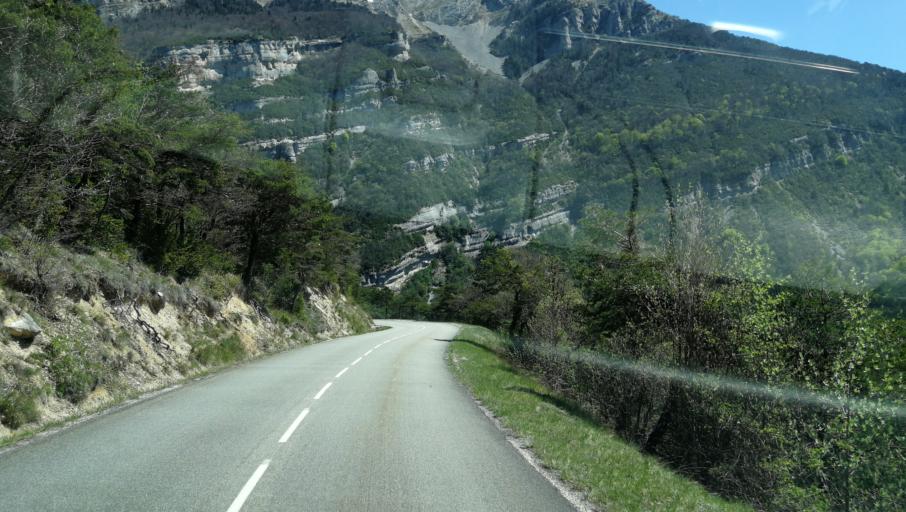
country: FR
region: Rhone-Alpes
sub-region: Departement de la Drome
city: Die
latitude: 44.8216
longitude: 5.3925
